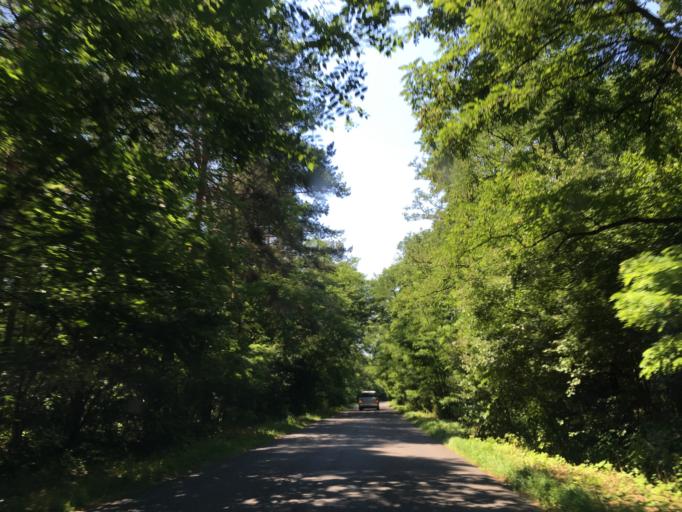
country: HU
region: Hajdu-Bihar
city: Mikepercs
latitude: 47.4687
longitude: 21.6876
